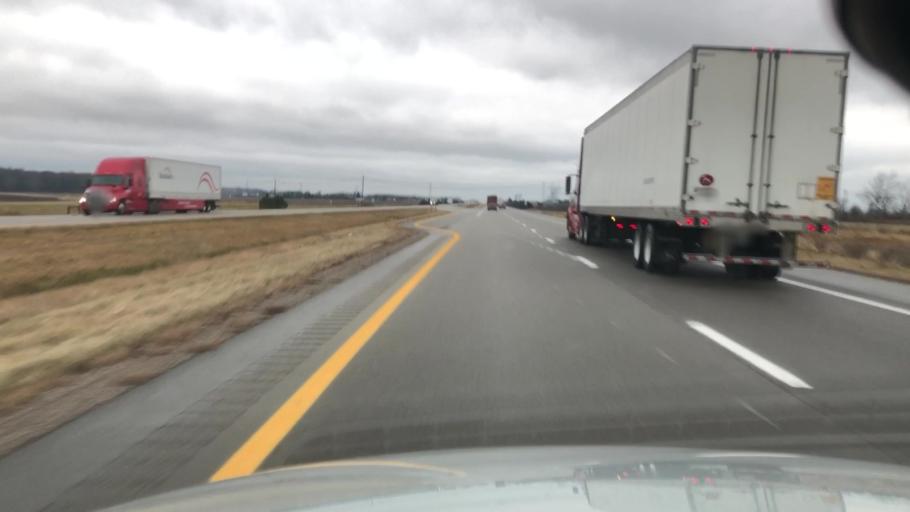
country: US
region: Ohio
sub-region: Van Wert County
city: Convoy
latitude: 40.9158
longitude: -84.6704
